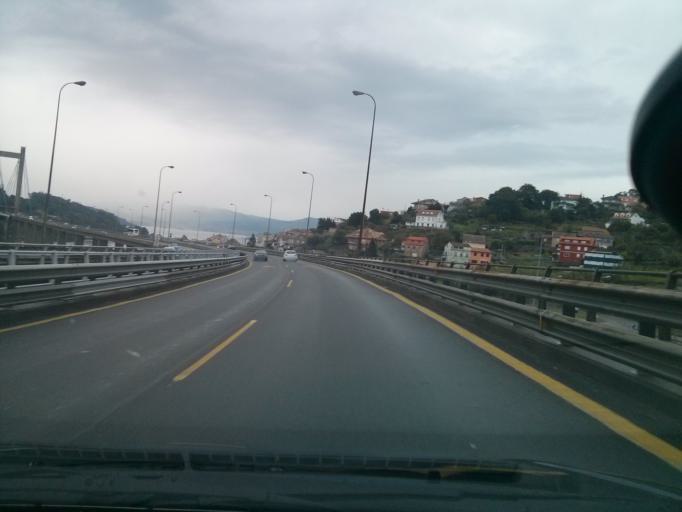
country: ES
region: Galicia
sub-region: Provincia de Pontevedra
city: Redondela
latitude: 42.2795
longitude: -8.6625
